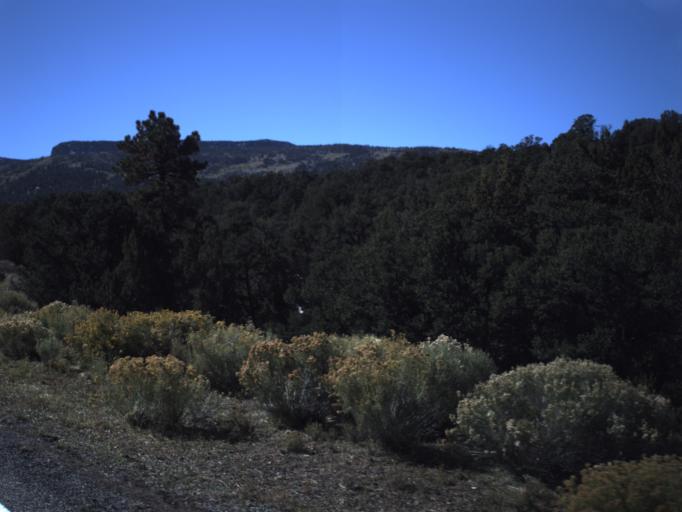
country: US
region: Utah
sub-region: Wayne County
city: Loa
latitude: 38.1995
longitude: -111.3511
